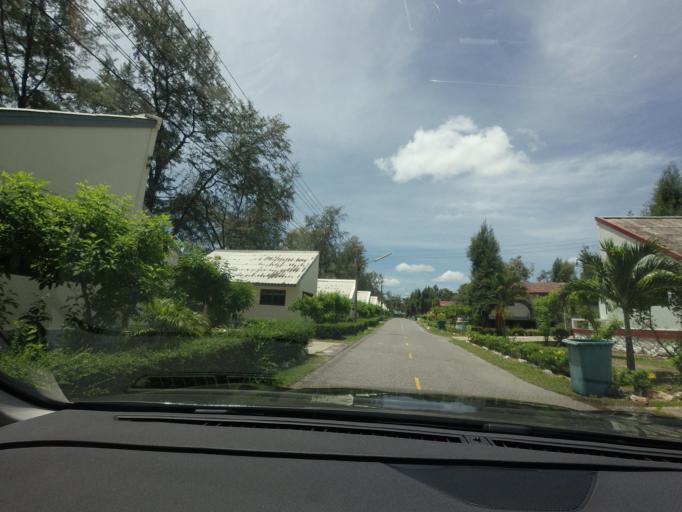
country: TH
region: Prachuap Khiri Khan
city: Hua Hin
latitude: 12.5003
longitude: 99.9741
